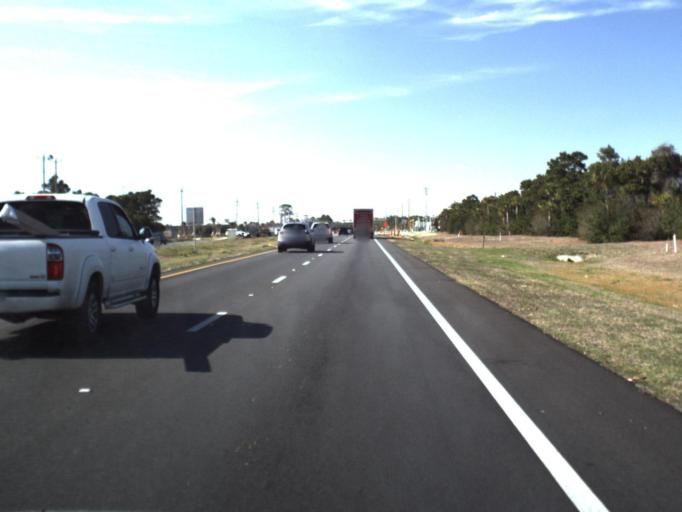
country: US
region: Florida
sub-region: Bay County
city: Laguna Beach
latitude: 30.2182
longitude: -85.8615
